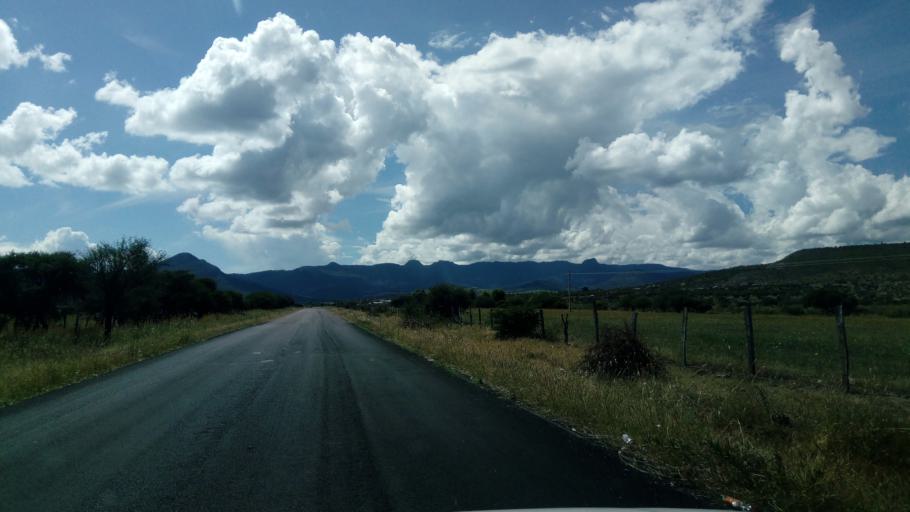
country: MX
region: Durango
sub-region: Durango
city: Jose Refugio Salcido
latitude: 23.8040
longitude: -104.4843
